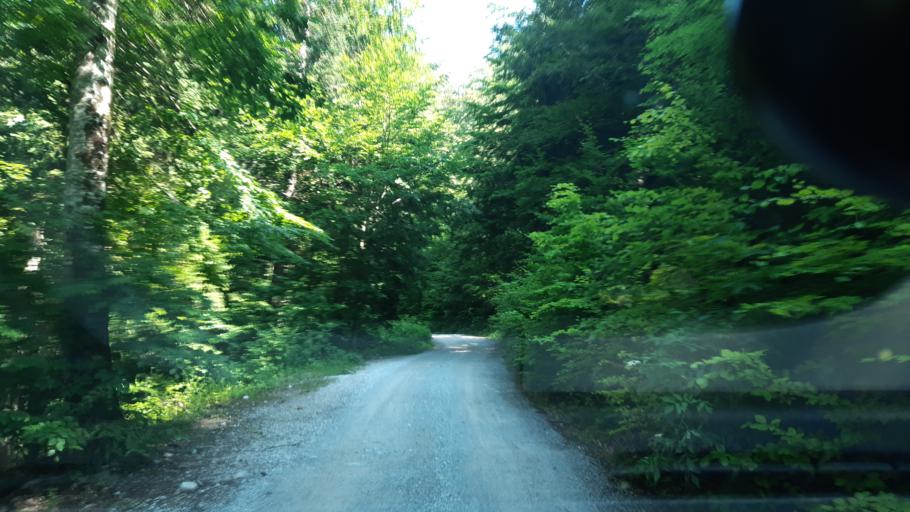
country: SI
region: Trzic
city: Bistrica pri Trzicu
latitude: 46.3761
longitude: 14.2763
